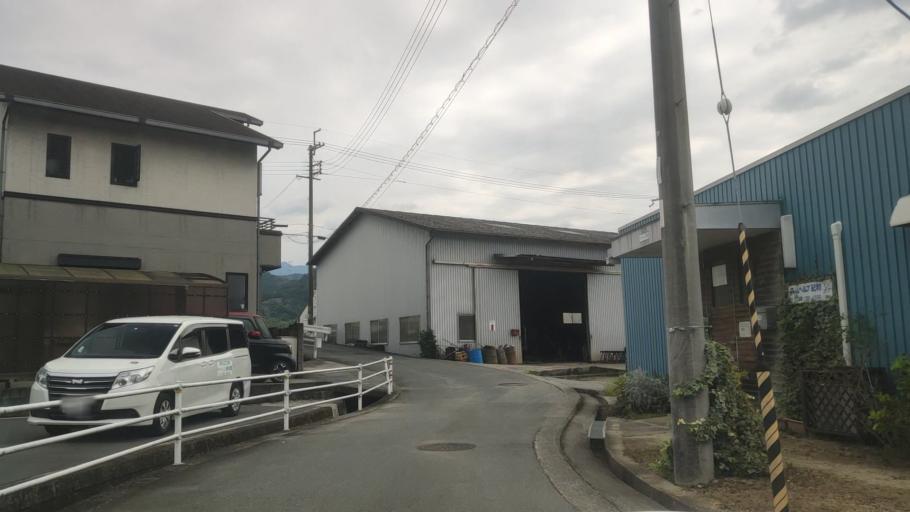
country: JP
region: Wakayama
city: Hashimoto
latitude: 34.3045
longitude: 135.5821
